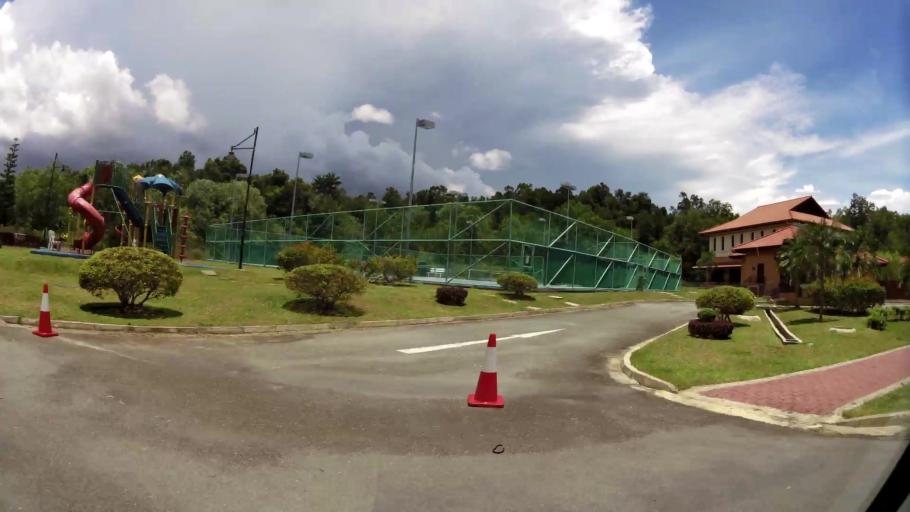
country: BN
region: Brunei and Muara
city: Bandar Seri Begawan
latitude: 4.9532
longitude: 114.8919
